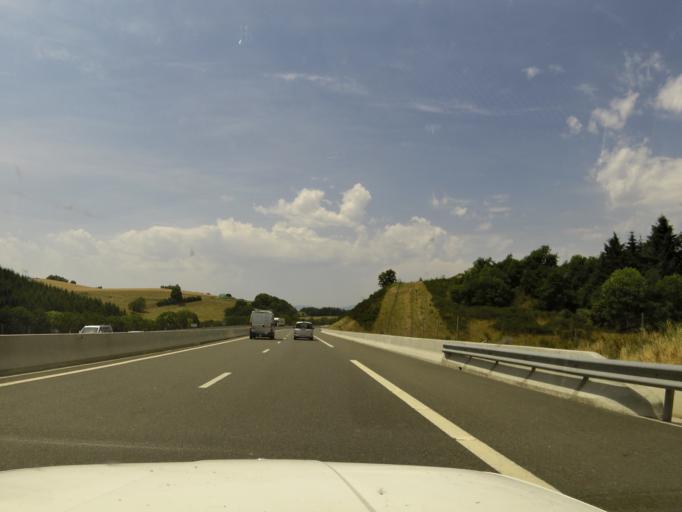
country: FR
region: Rhone-Alpes
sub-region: Departement de la Loire
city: Saint-Just-la-Pendue
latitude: 45.8642
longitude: 4.2483
